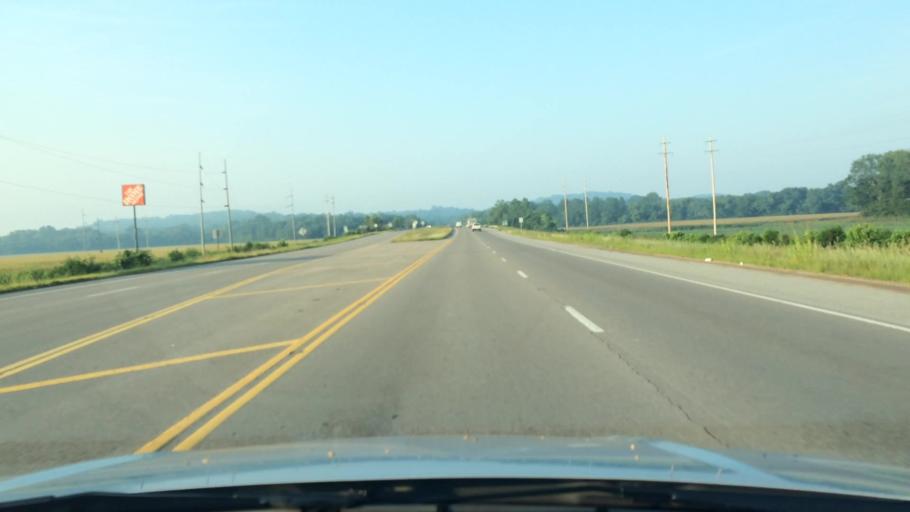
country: US
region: Tennessee
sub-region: Giles County
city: Pulaski
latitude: 35.2033
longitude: -87.0631
